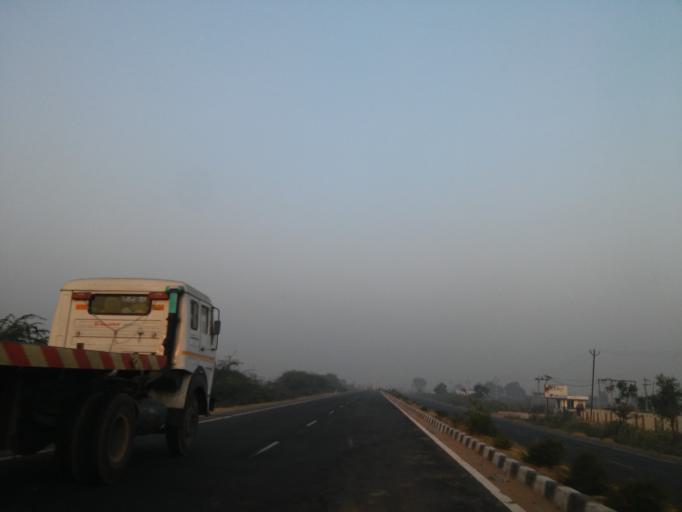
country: IN
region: Gujarat
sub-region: Surendranagar
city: Halvad
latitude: 23.0179
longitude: 71.0102
